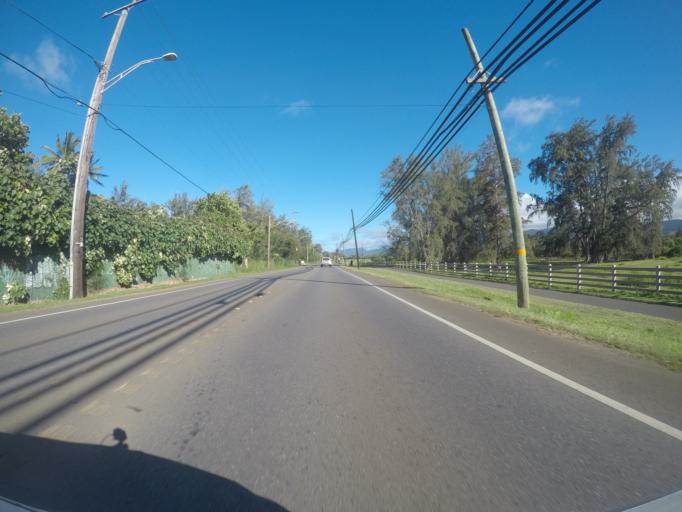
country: US
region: Hawaii
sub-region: Honolulu County
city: La'ie
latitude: 21.6632
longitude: -157.9355
